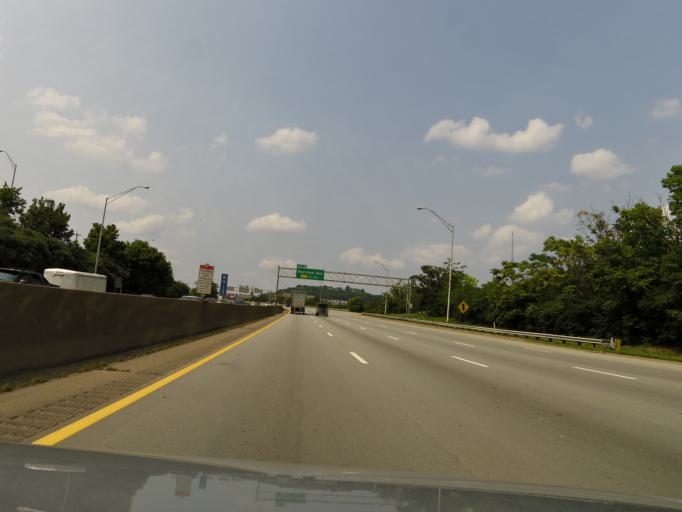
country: US
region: Kentucky
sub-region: Kenton County
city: Ludlow
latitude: 39.1103
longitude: -84.5315
